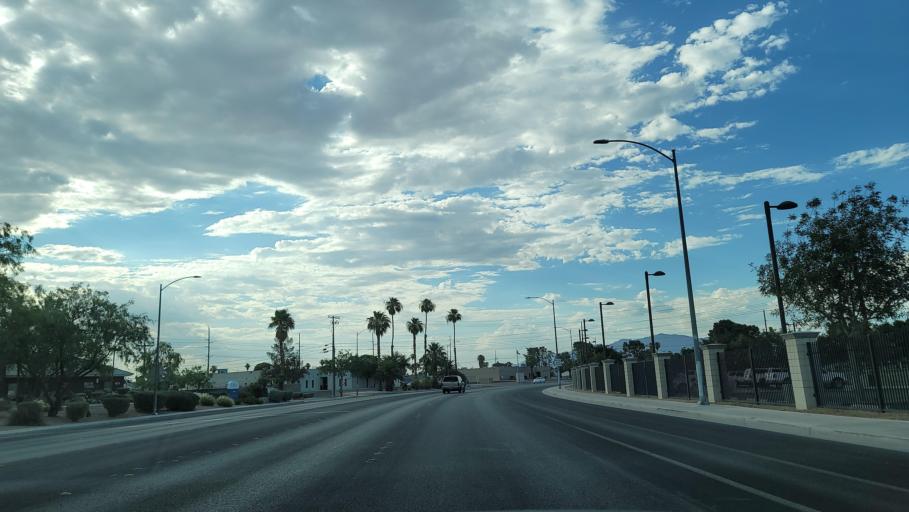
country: US
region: Nevada
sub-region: Clark County
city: North Las Vegas
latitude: 36.1784
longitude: -115.1064
